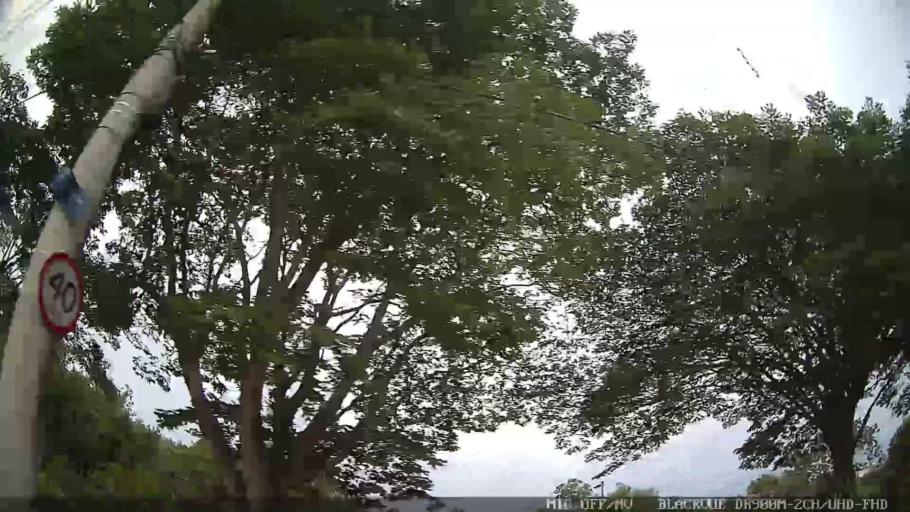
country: BR
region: Sao Paulo
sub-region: Braganca Paulista
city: Braganca Paulista
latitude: -22.9617
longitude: -46.5470
